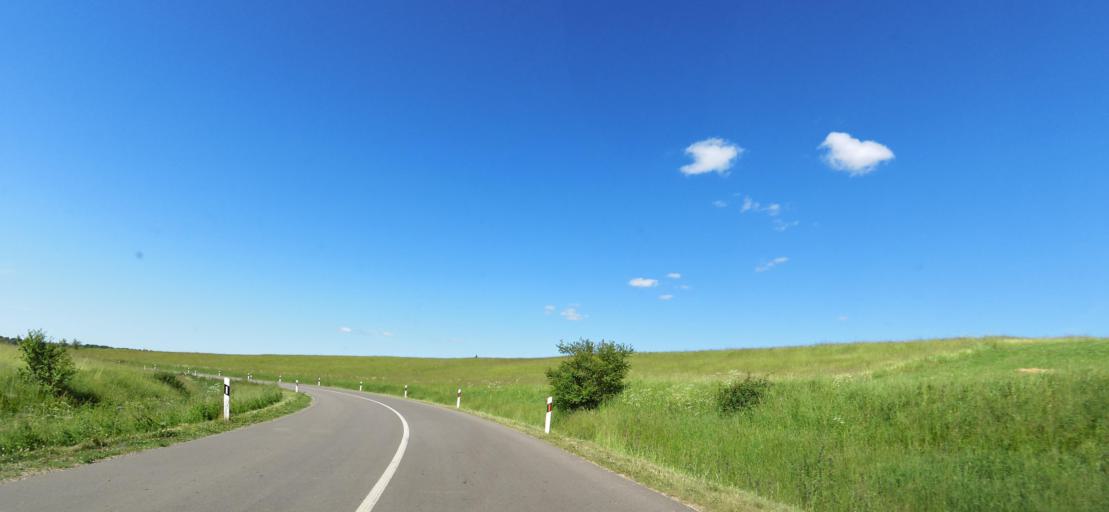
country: LT
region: Utenos apskritis
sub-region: Anyksciai
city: Anyksciai
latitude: 55.3568
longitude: 25.1208
